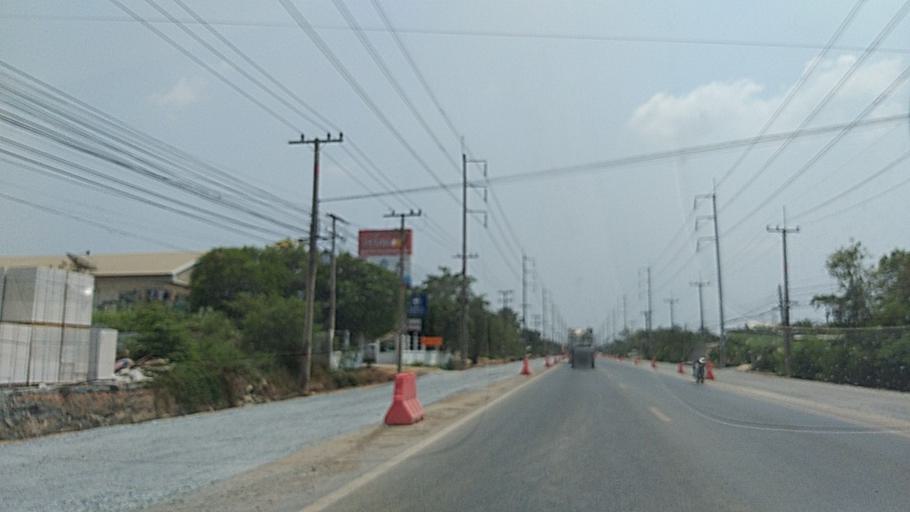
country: TH
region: Chachoengsao
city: Ban Pho
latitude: 13.6125
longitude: 101.1130
